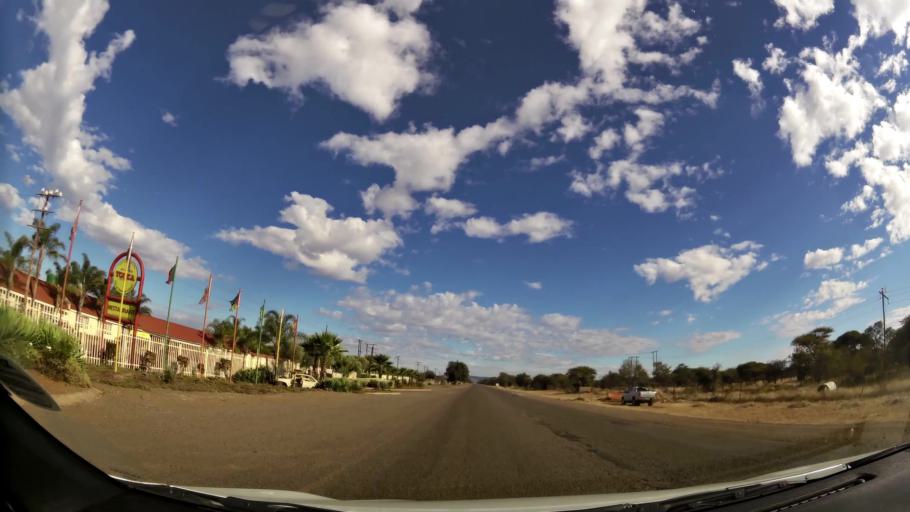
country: ZA
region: Limpopo
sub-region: Waterberg District Municipality
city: Bela-Bela
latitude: -24.9138
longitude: 28.3605
